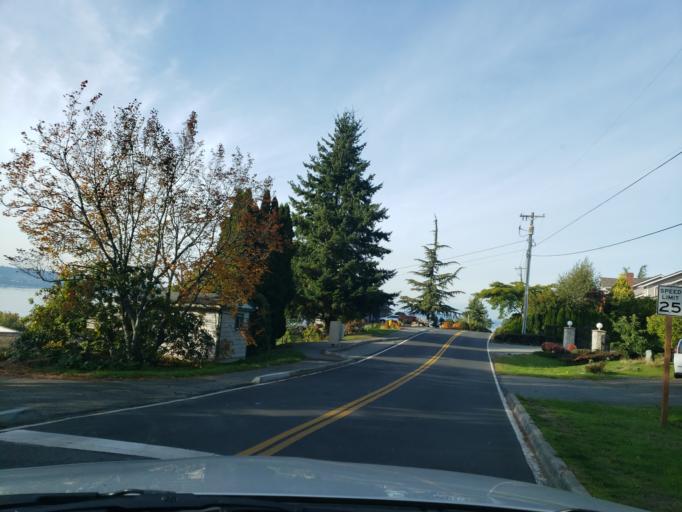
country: US
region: Washington
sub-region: Snohomish County
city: Mukilteo
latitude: 47.9404
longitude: -122.3041
